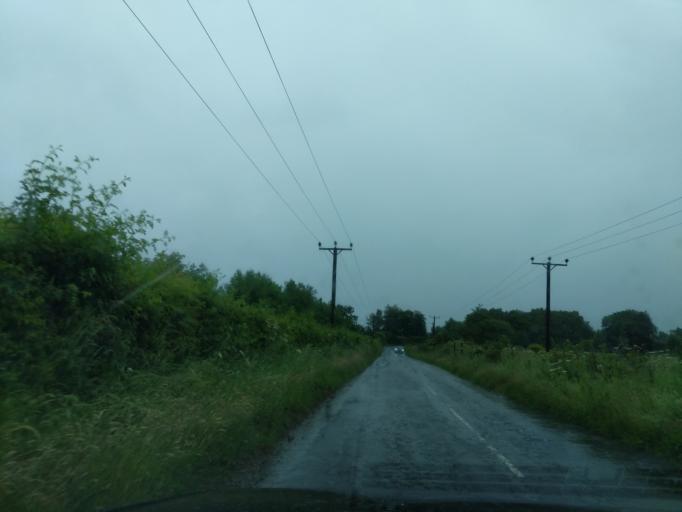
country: GB
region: Scotland
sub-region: Midlothian
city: Loanhead
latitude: 55.8519
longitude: -3.1791
